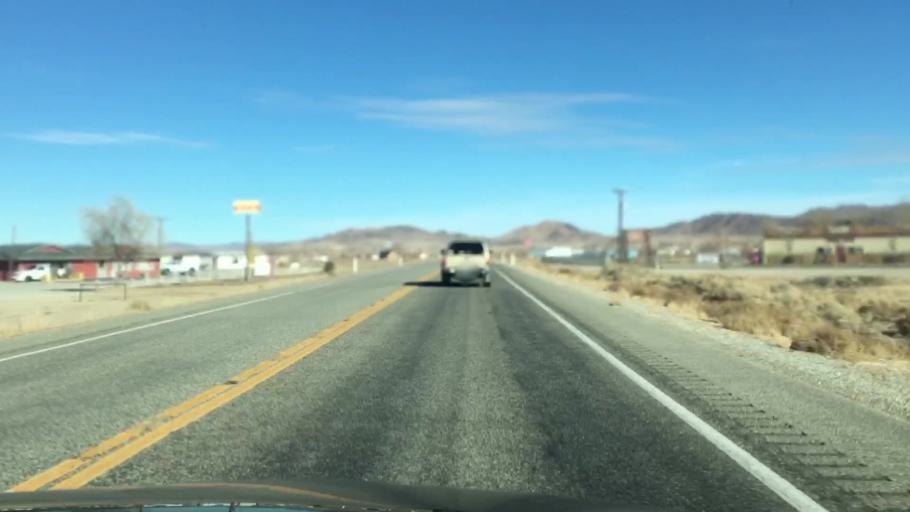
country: US
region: Nevada
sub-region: Lyon County
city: Yerington
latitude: 39.0091
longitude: -119.0802
